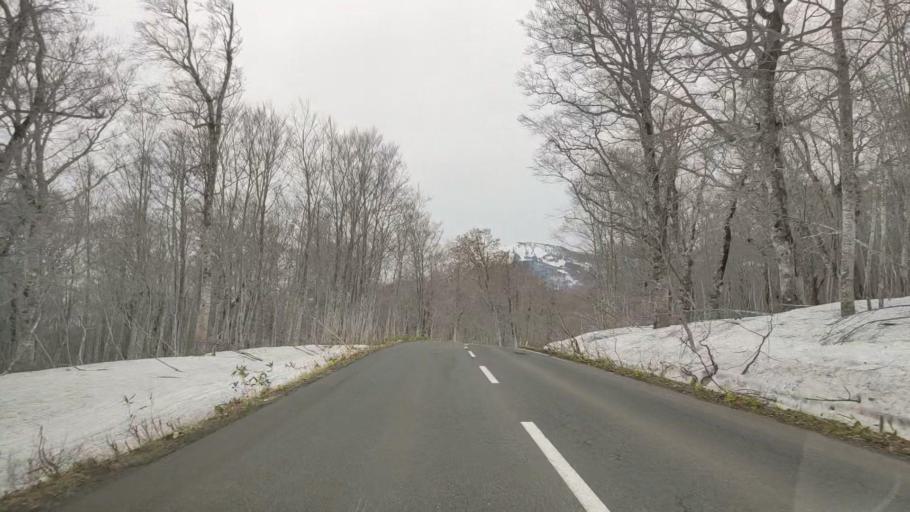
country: JP
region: Aomori
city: Aomori Shi
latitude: 40.6396
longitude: 140.9322
